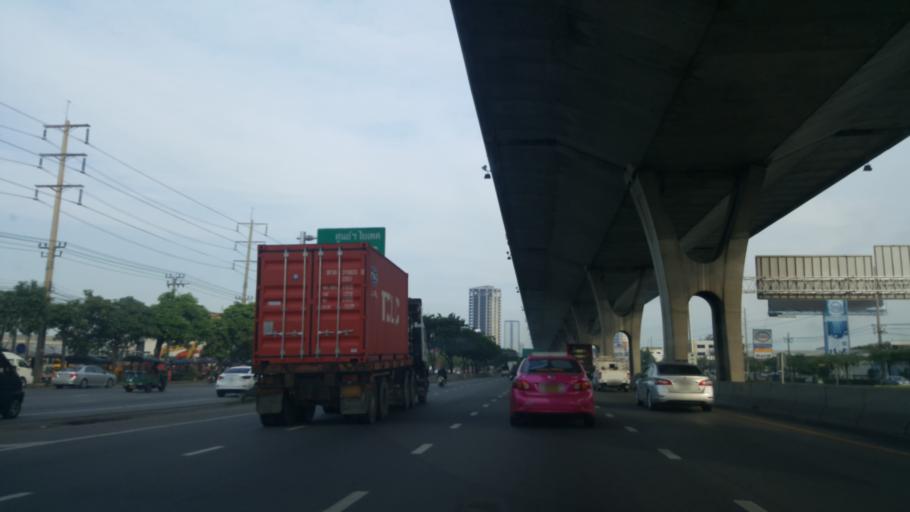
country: TH
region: Bangkok
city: Bang Na
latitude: 13.6720
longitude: 100.6159
